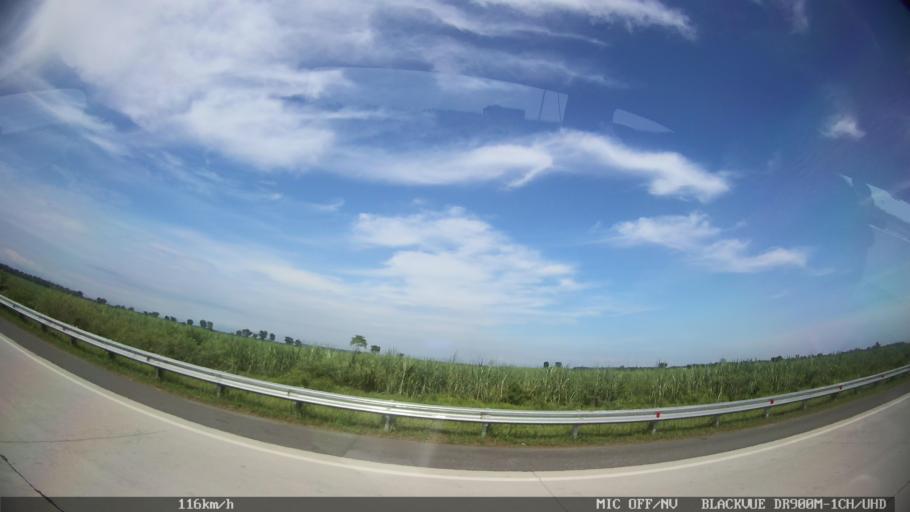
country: ID
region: North Sumatra
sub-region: Kabupaten Langkat
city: Stabat
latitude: 3.6942
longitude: 98.5409
